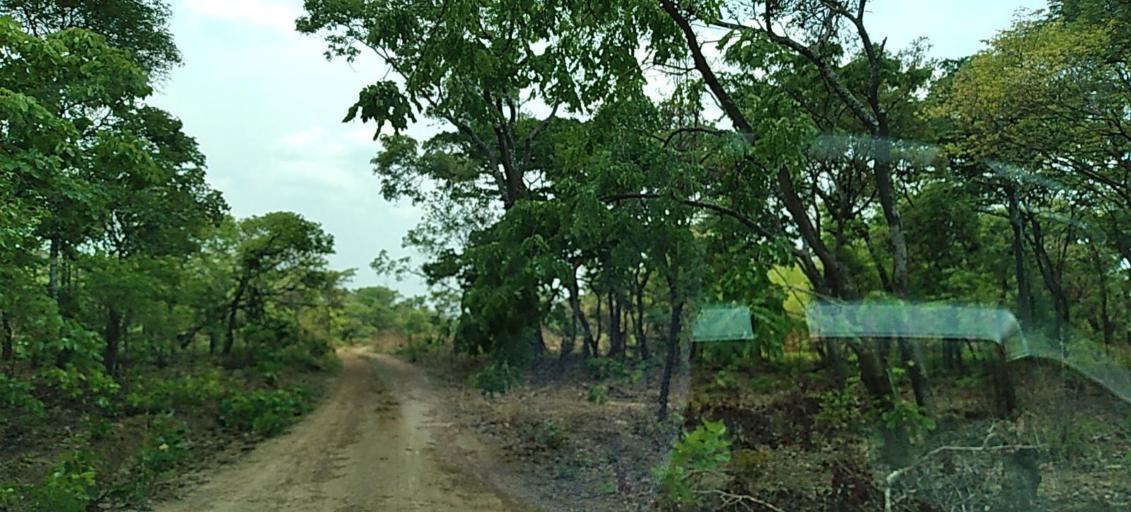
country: ZM
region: Copperbelt
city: Chililabombwe
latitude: -12.3808
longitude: 27.6445
